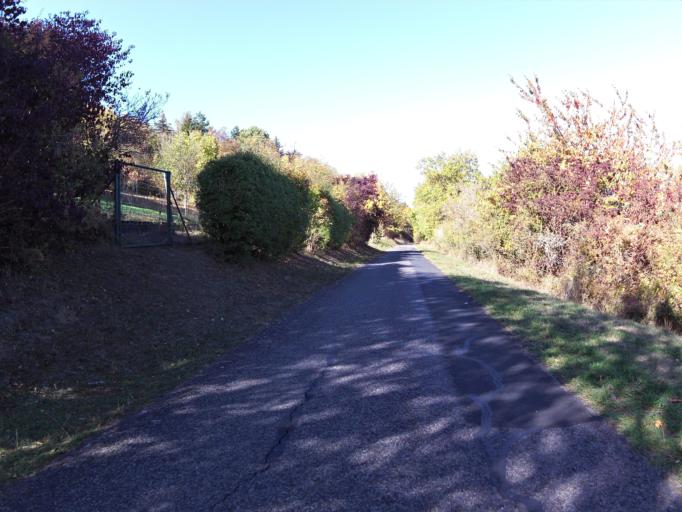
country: DE
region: Bavaria
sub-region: Regierungsbezirk Unterfranken
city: Eibelstadt
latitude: 49.7208
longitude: 9.9898
